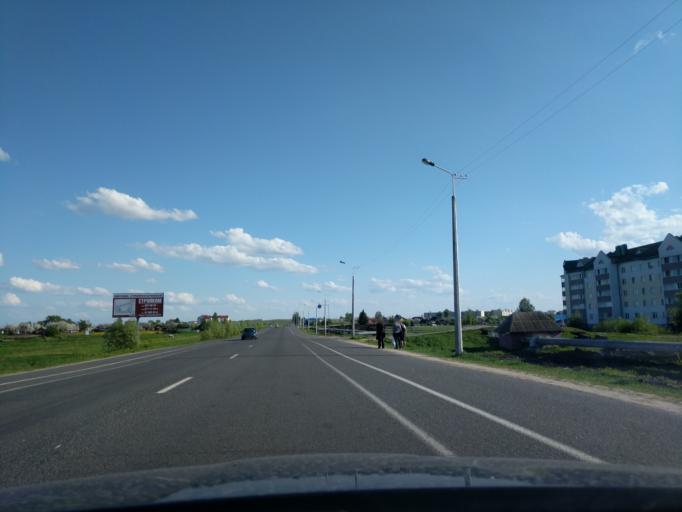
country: BY
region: Minsk
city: Myadzyel
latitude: 54.8817
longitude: 26.9392
